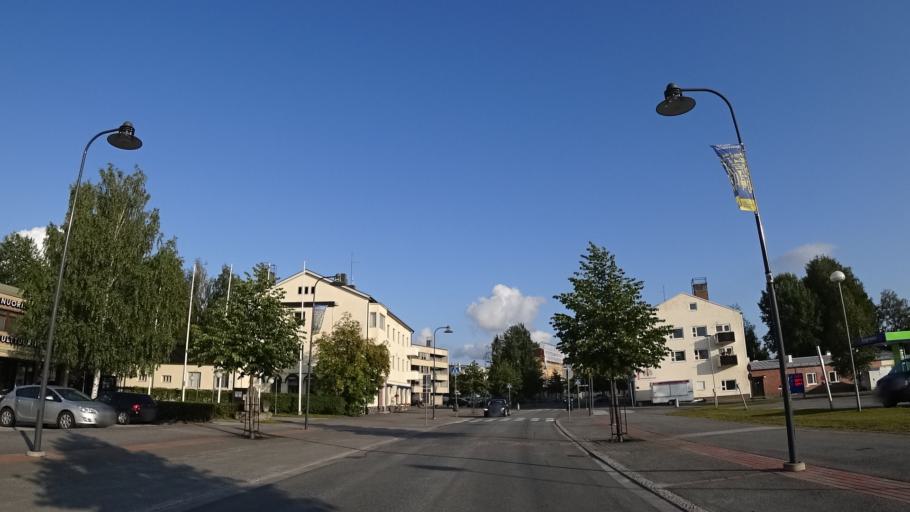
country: FI
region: North Karelia
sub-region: Pielisen Karjala
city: Lieksa
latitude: 63.3167
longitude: 30.0312
